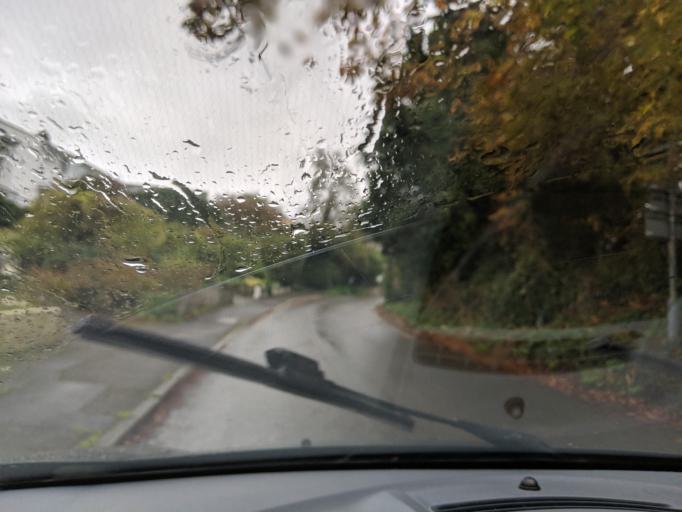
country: GB
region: England
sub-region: Cornwall
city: Wadebridge
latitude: 50.5163
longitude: -4.8215
